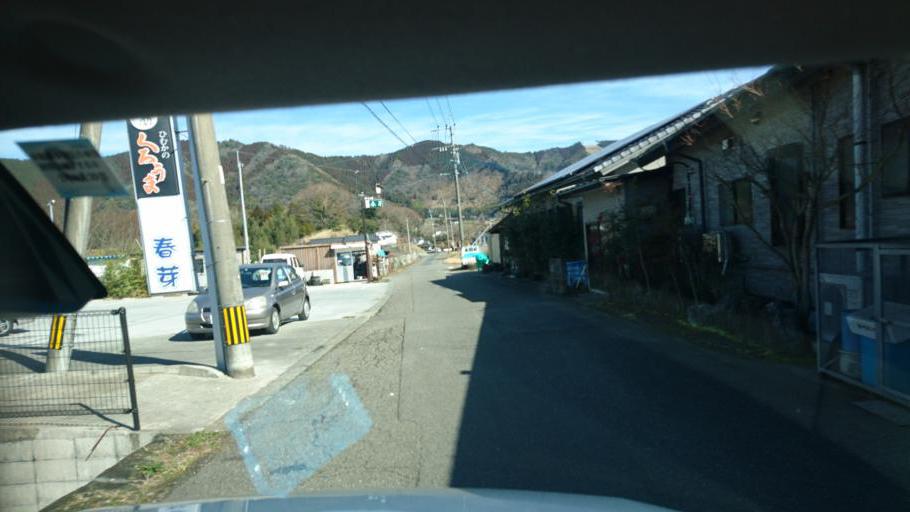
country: JP
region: Oita
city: Takedamachi
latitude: 32.6869
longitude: 131.3492
